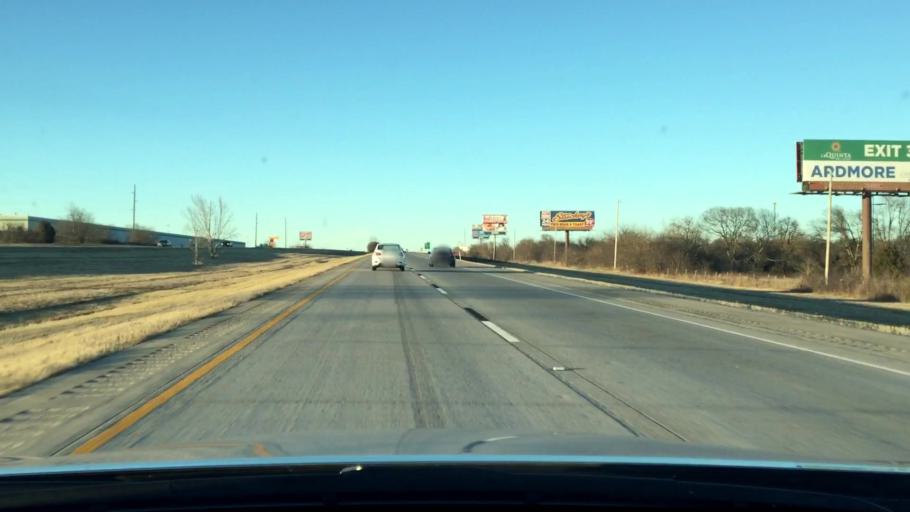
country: US
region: Oklahoma
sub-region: Love County
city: Marietta
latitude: 33.9300
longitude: -97.1346
